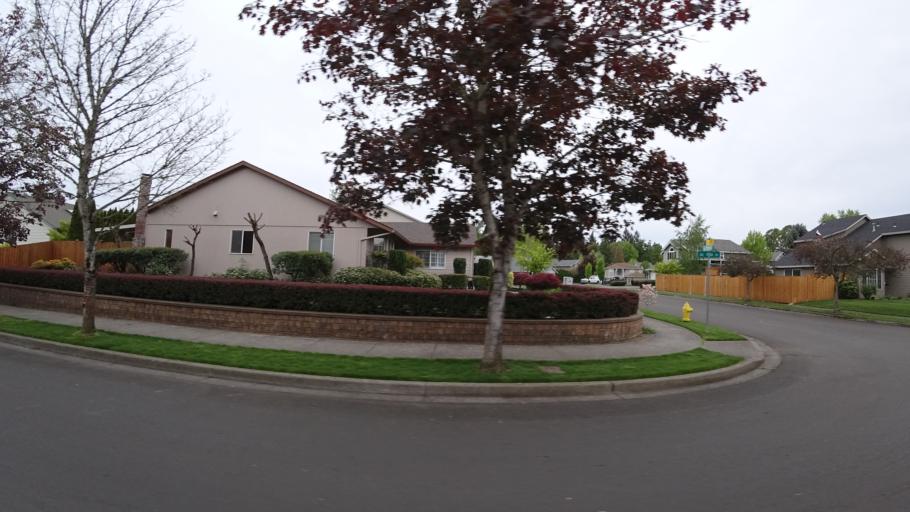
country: US
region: Oregon
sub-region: Washington County
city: Aloha
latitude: 45.5064
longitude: -122.9074
